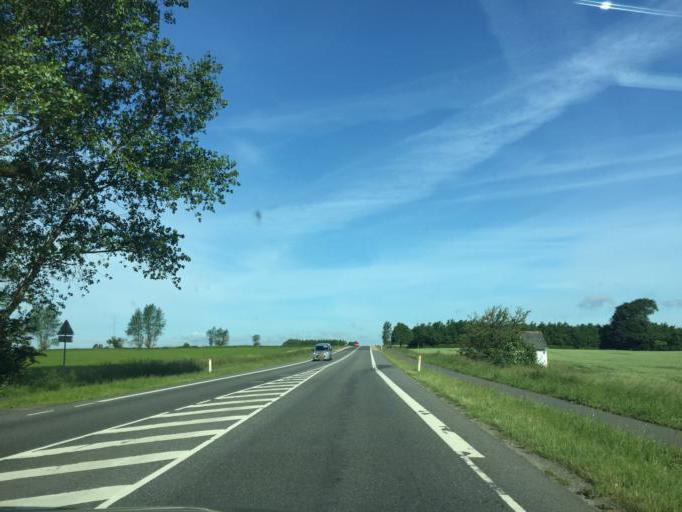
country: DK
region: South Denmark
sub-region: Middelfart Kommune
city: Norre Aby
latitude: 55.4791
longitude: 9.8508
